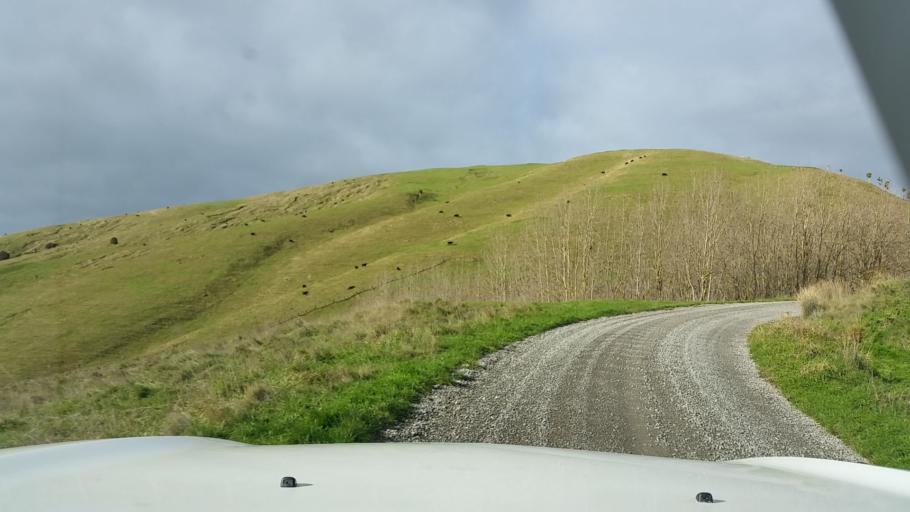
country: NZ
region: Wellington
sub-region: Masterton District
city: Masterton
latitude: -41.0346
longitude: 175.7119
